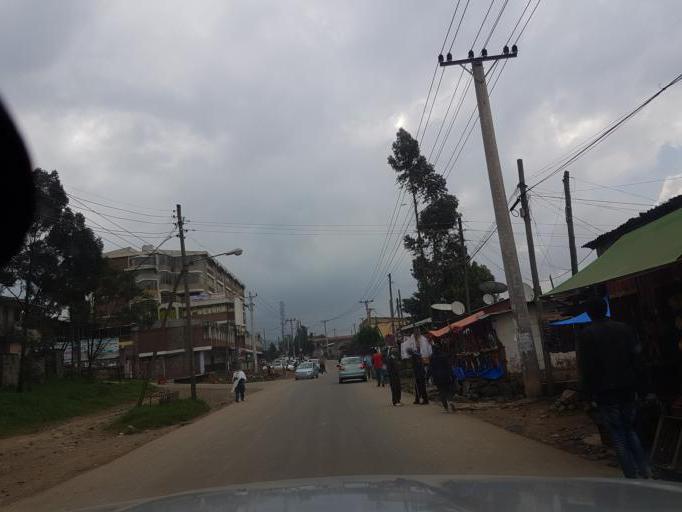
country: ET
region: Adis Abeba
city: Addis Ababa
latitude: 9.0226
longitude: 38.7658
